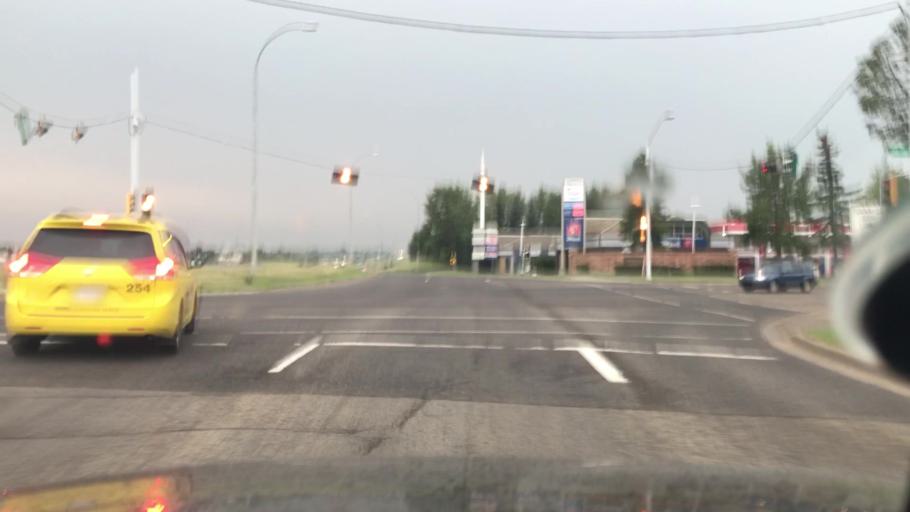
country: CA
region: Alberta
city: Edmonton
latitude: 53.4769
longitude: -113.5755
